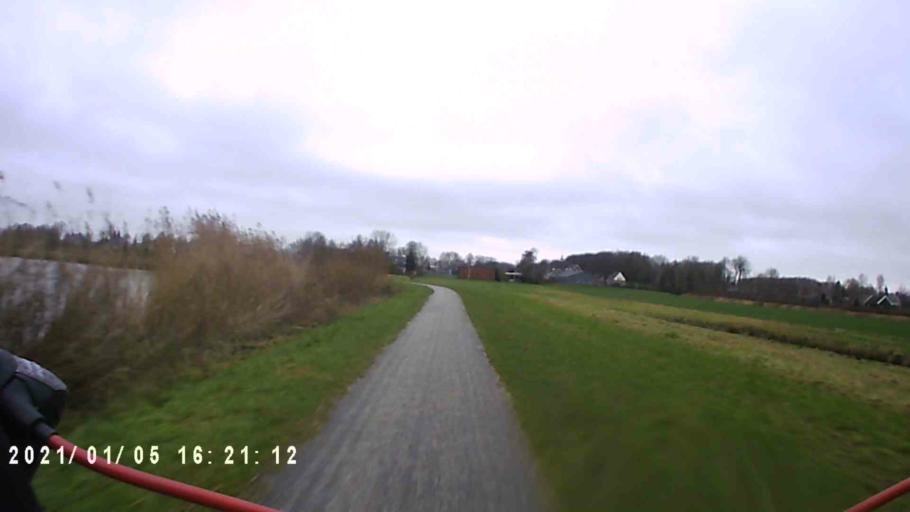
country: NL
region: Groningen
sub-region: Gemeente  Oldambt
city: Winschoten
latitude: 53.1992
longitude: 7.0432
